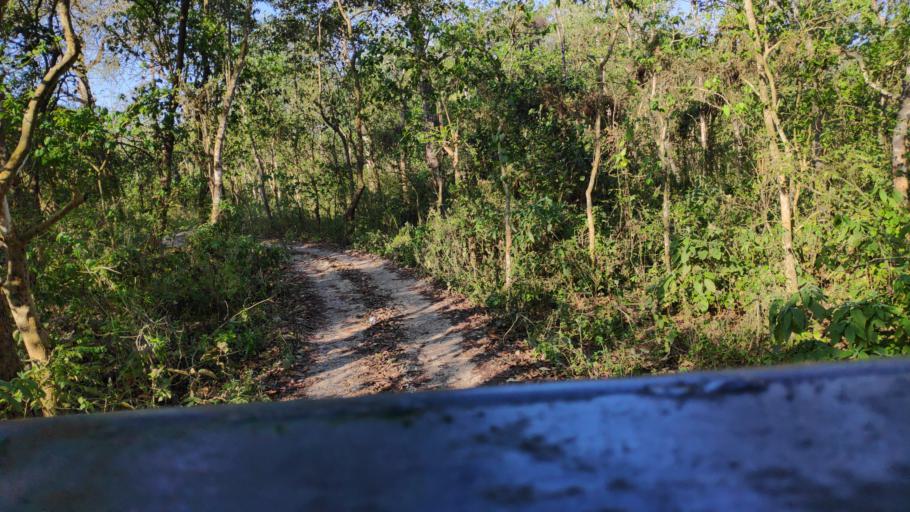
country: NP
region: Central Region
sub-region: Narayani Zone
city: Bharatpur
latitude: 27.5592
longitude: 84.5468
